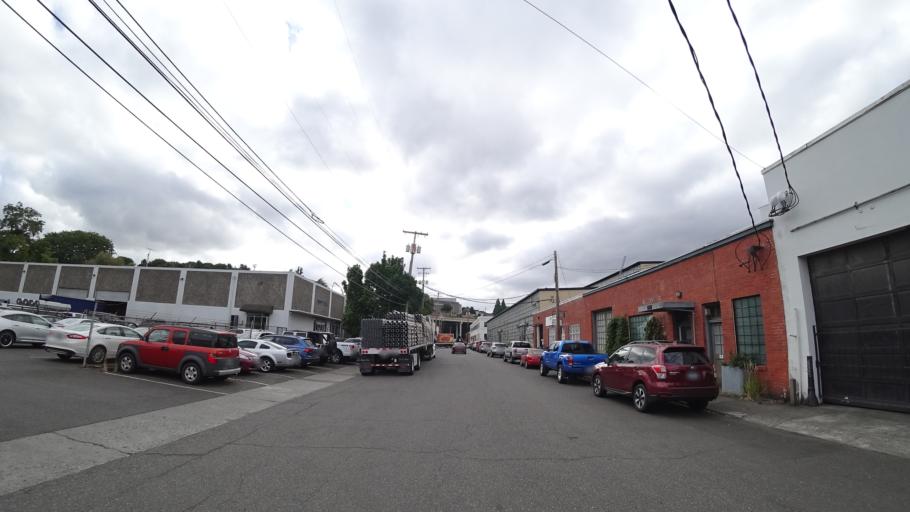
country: US
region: Oregon
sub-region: Multnomah County
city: Portland
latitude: 45.5387
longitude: -122.6731
